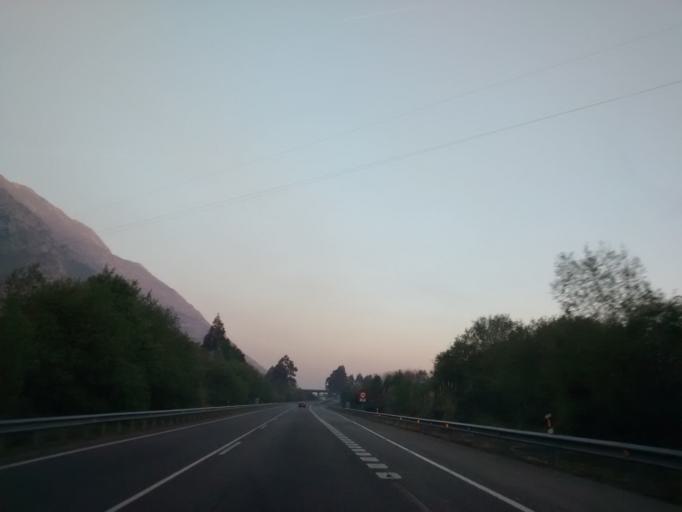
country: ES
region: Asturias
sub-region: Province of Asturias
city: Ribadesella
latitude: 43.4364
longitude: -5.0074
